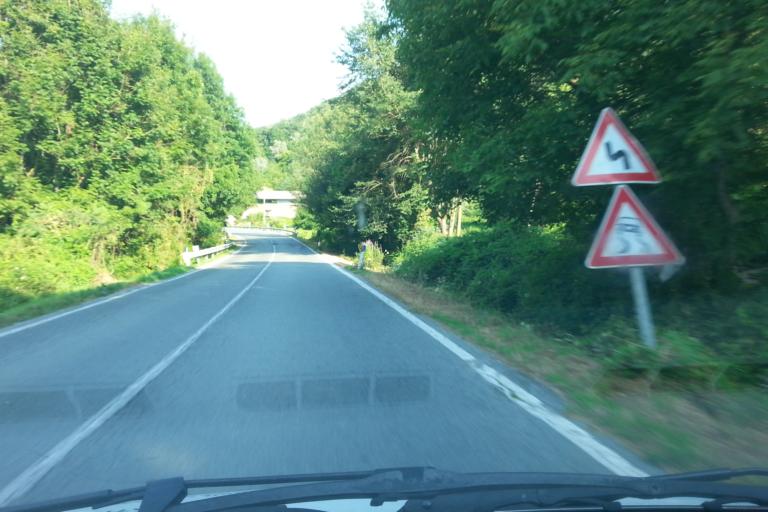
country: IT
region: Piedmont
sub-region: Provincia di Torino
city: Bruzolo
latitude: 45.1220
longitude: 7.1951
